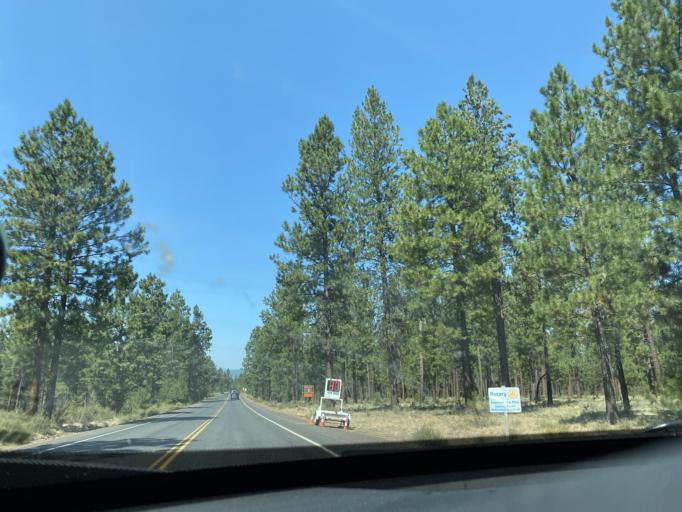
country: US
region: Oregon
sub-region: Deschutes County
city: Sunriver
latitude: 43.8928
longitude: -121.4117
